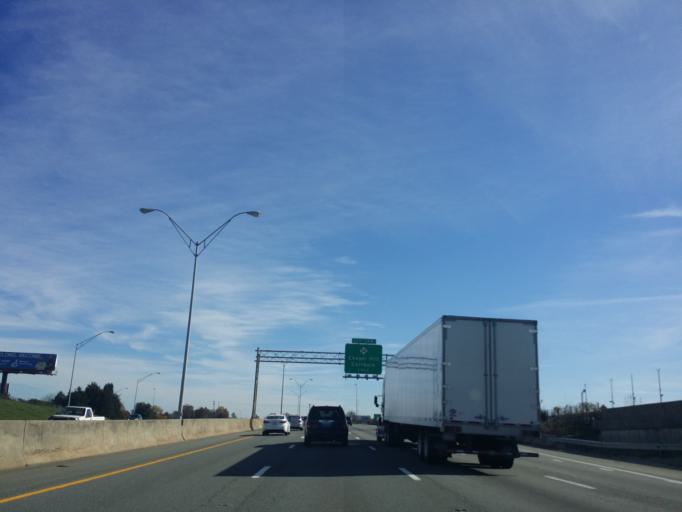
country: US
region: North Carolina
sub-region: Alamance County
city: Graham
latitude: 36.0605
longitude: -79.4050
